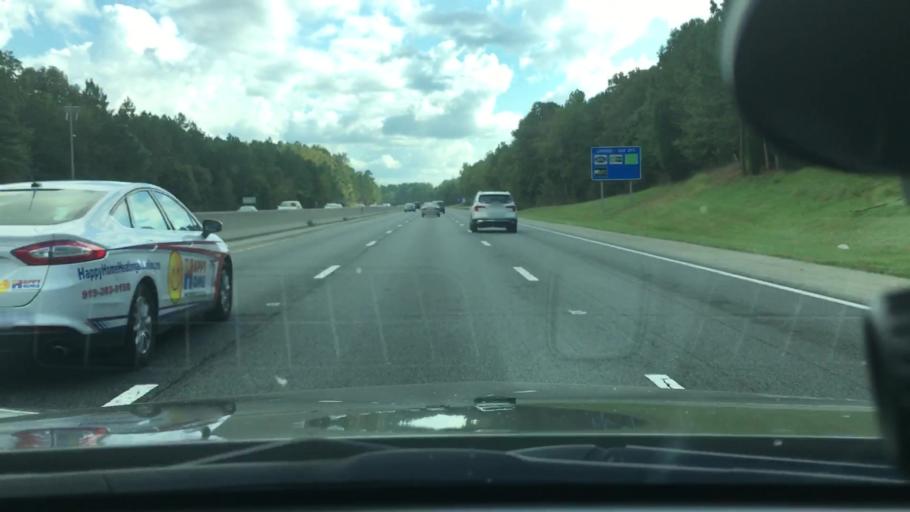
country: US
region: North Carolina
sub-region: Orange County
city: Chapel Hill
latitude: 35.9253
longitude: -78.9863
